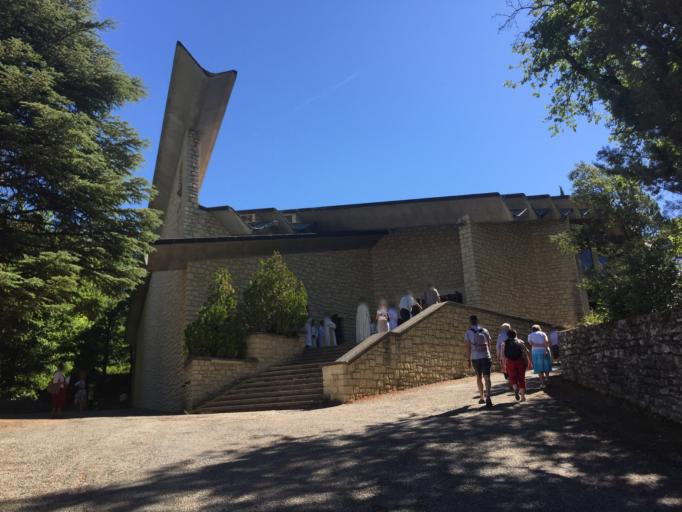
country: FR
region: Provence-Alpes-Cote d'Azur
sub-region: Departement du Vaucluse
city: Venasque
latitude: 44.0012
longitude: 5.1468
